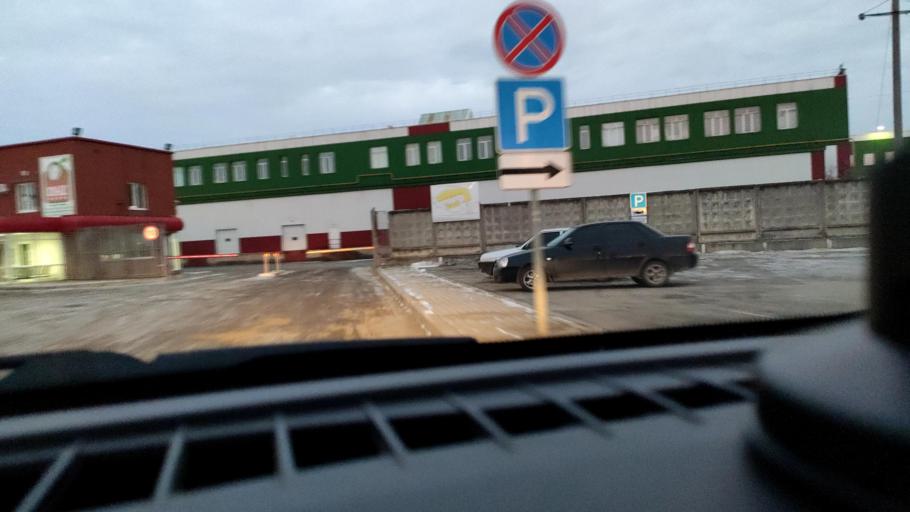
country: RU
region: Perm
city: Kondratovo
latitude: 58.0077
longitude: 56.1497
